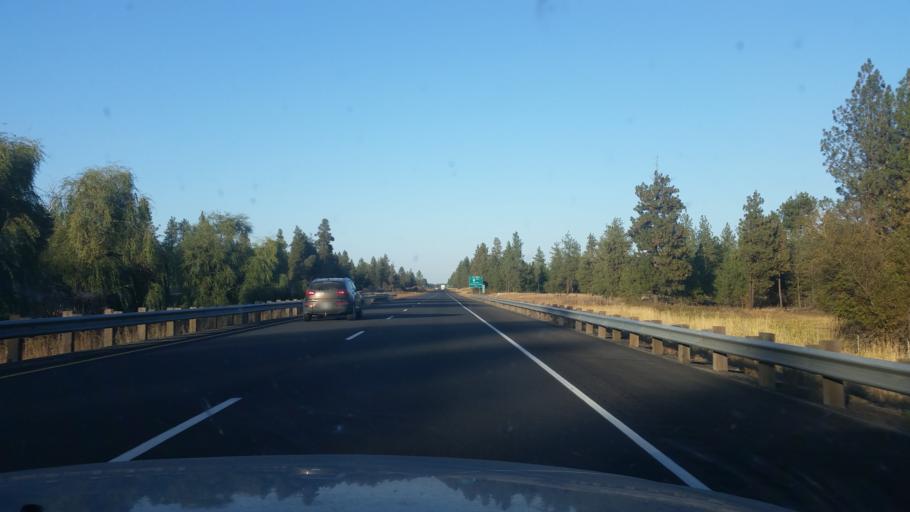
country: US
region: Washington
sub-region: Spokane County
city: Medical Lake
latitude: 47.4899
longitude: -117.7118
